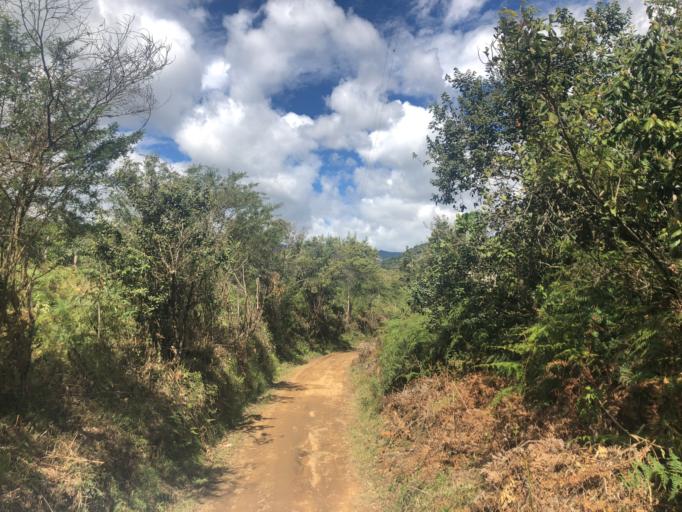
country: CO
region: Cauca
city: Silvia
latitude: 2.6826
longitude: -76.4368
